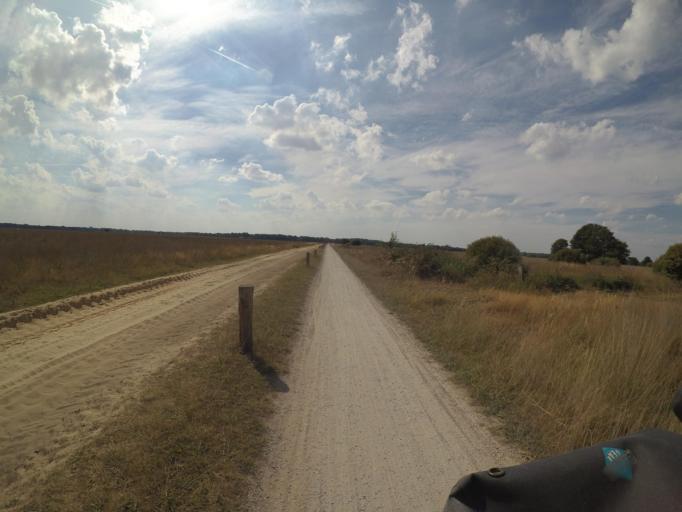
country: NL
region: Drenthe
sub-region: Gemeente De Wolden
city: Ruinen
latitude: 52.7921
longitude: 6.3894
